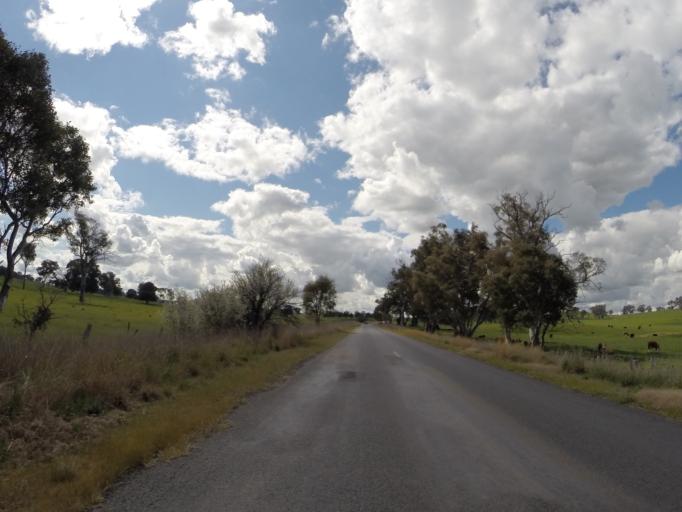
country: AU
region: New South Wales
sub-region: Yass Valley
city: Yass
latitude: -34.9287
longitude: 148.8770
